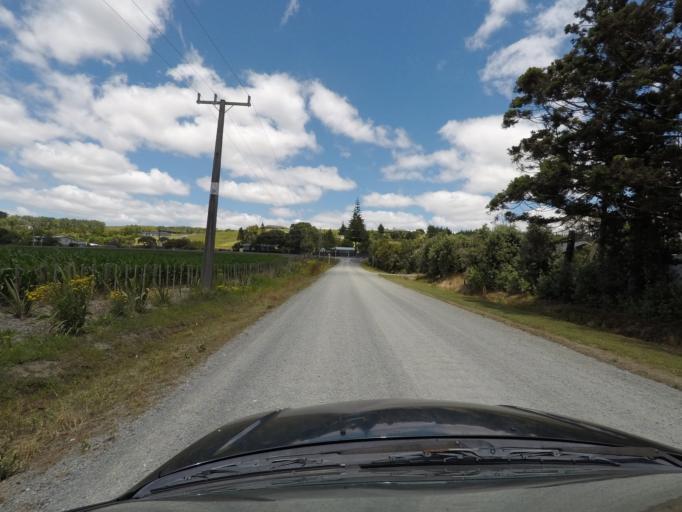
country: NZ
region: Northland
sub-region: Whangarei
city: Ruakaka
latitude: -35.9996
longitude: 174.4762
